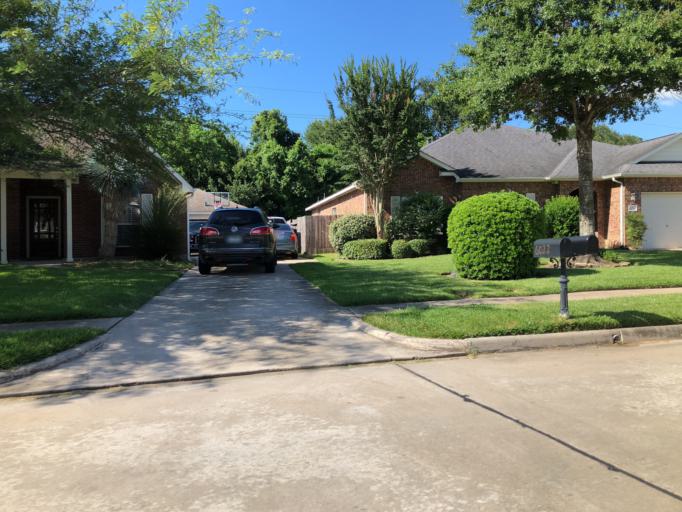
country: US
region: Texas
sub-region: Harris County
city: Katy
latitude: 29.8084
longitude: -95.8284
